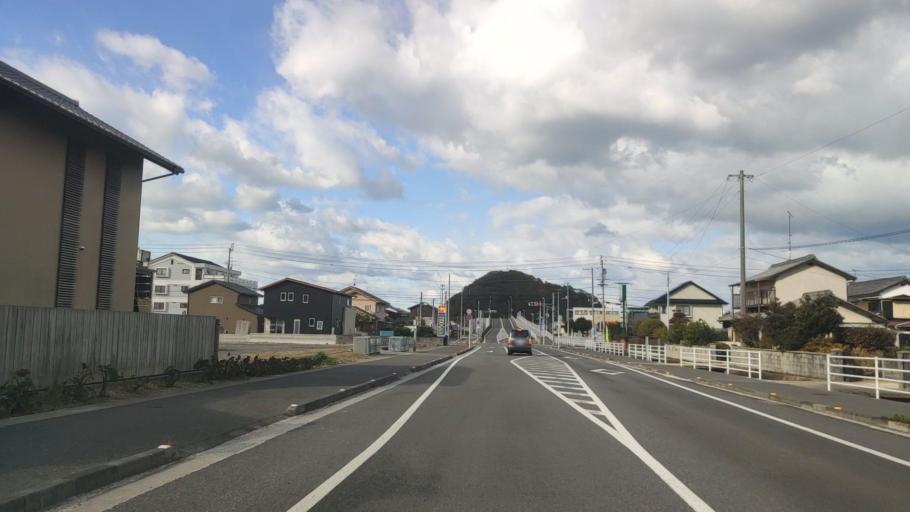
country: JP
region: Ehime
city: Hojo
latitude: 33.9709
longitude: 132.7777
